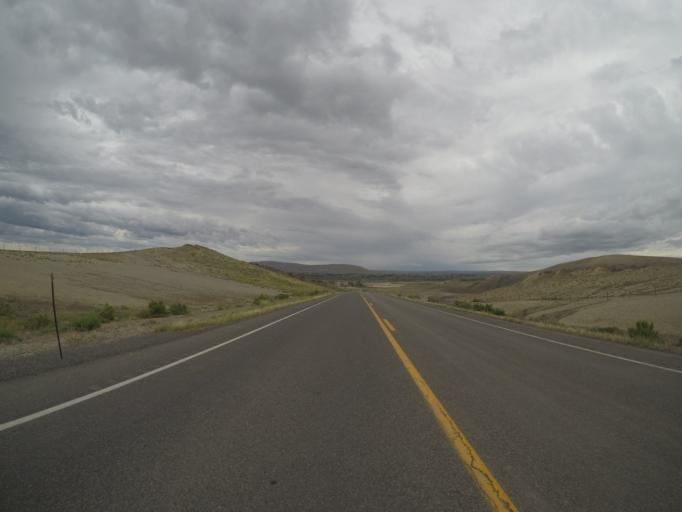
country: US
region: Wyoming
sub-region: Big Horn County
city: Lovell
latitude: 44.8872
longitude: -108.2888
